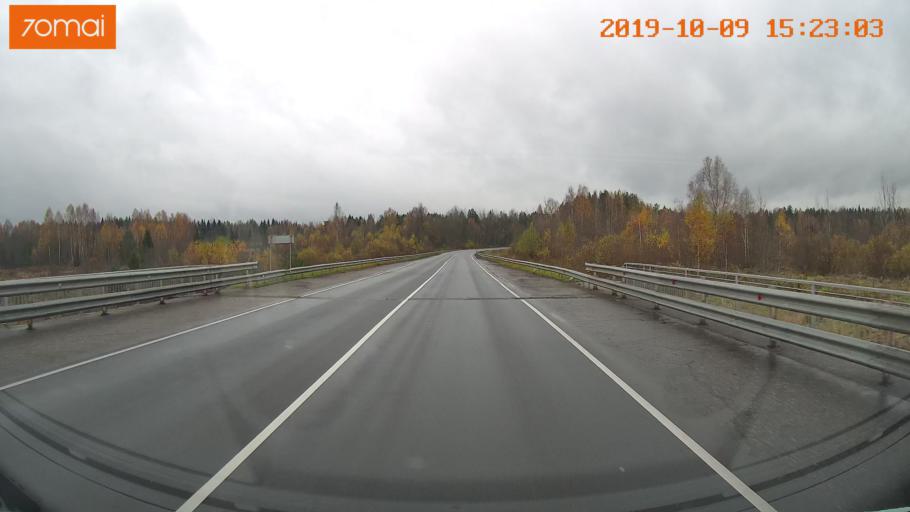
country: RU
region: Kostroma
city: Susanino
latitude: 58.0387
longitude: 41.4874
